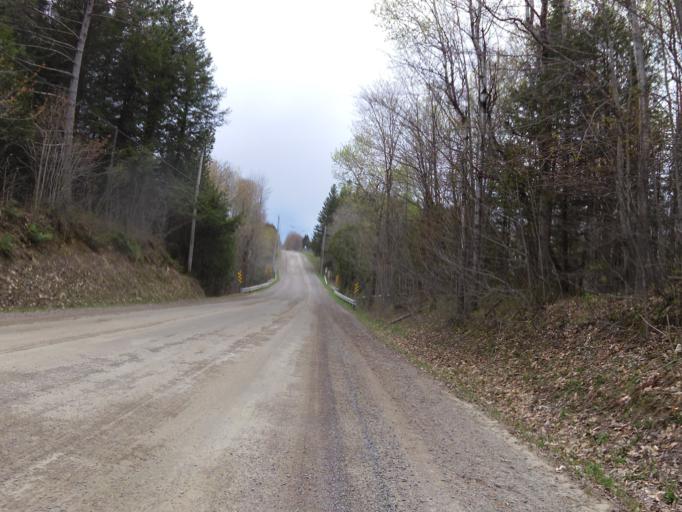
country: CA
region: Ontario
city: Hawkesbury
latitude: 45.6176
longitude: -74.5291
